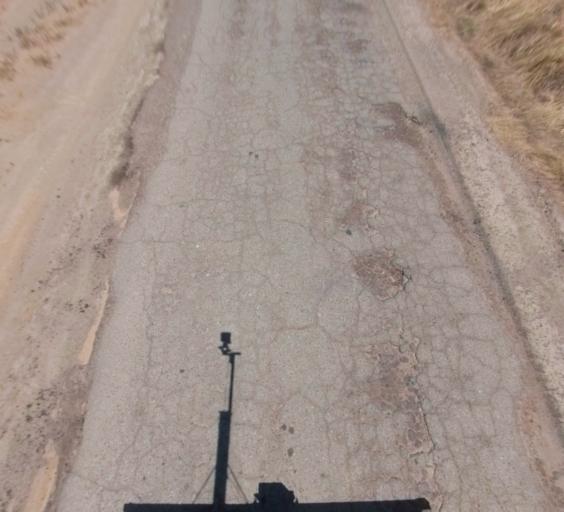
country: US
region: California
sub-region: Madera County
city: Bonadelle Ranchos-Madera Ranchos
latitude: 36.9343
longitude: -119.8306
